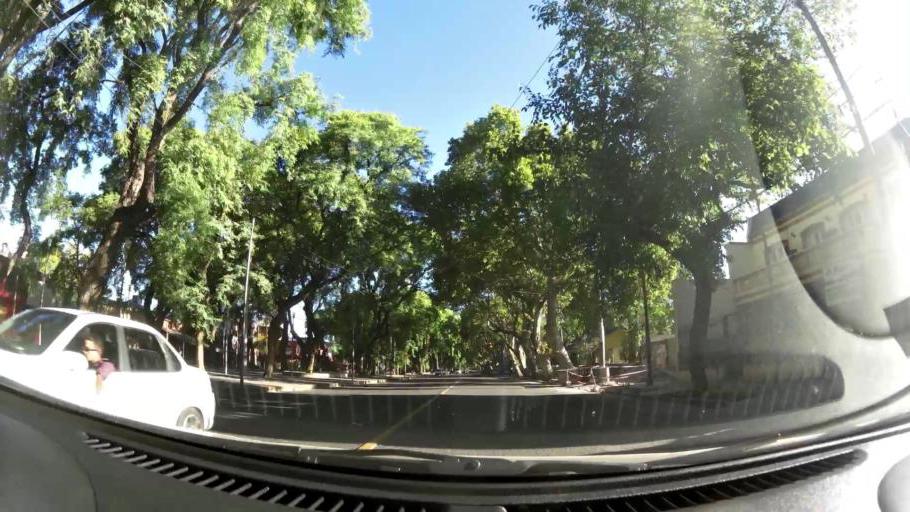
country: AR
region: Mendoza
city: Mendoza
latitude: -32.8756
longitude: -68.8355
